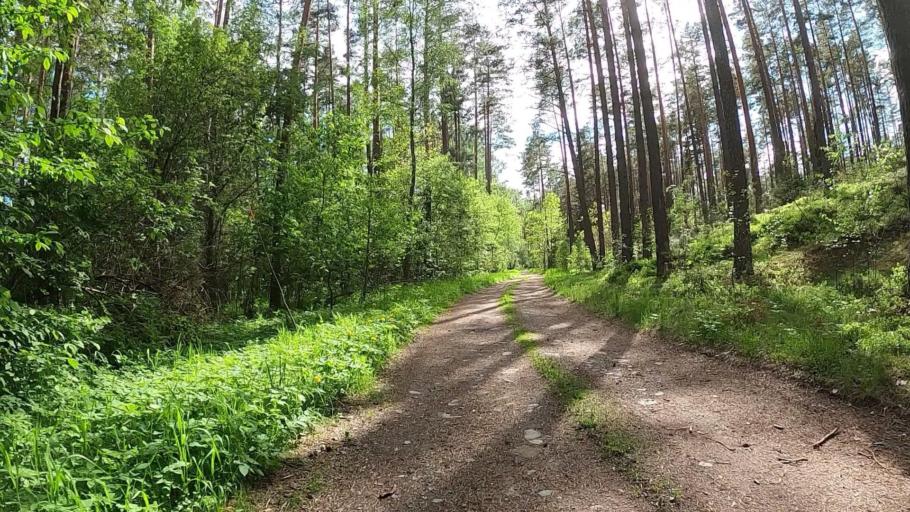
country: LV
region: Jurmala
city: Jurmala
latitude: 56.8992
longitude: 23.8237
